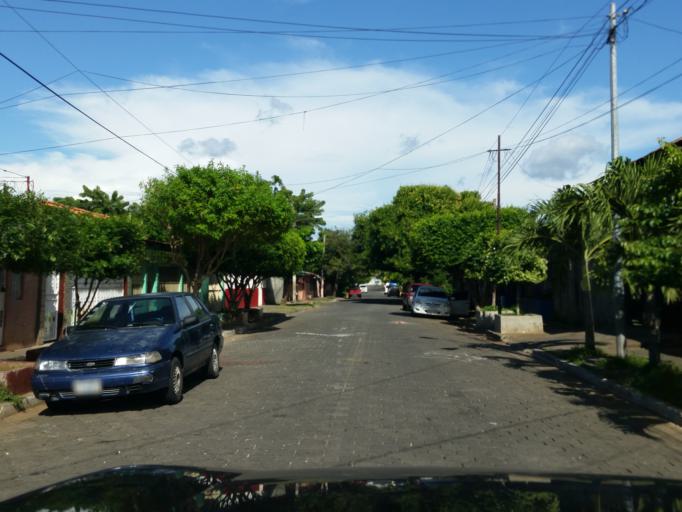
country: NI
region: Managua
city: Managua
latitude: 12.1417
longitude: -86.2411
